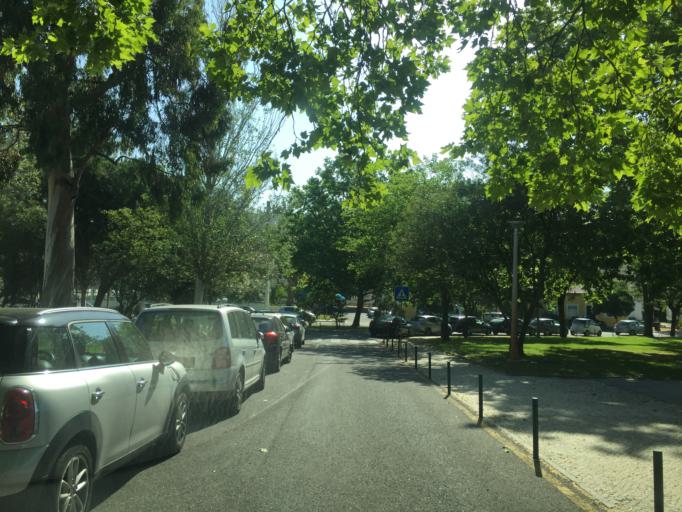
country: PT
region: Lisbon
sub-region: Odivelas
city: Olival do Basto
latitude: 38.7655
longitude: -9.1592
